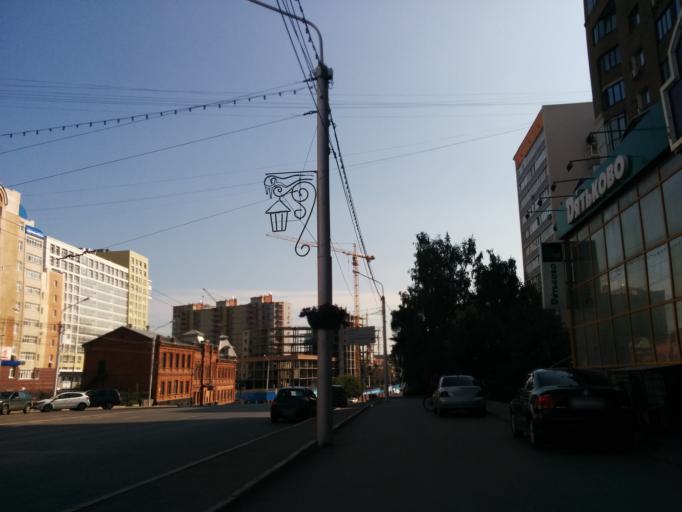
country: RU
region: Bashkortostan
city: Ufa
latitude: 54.7264
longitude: 55.9538
